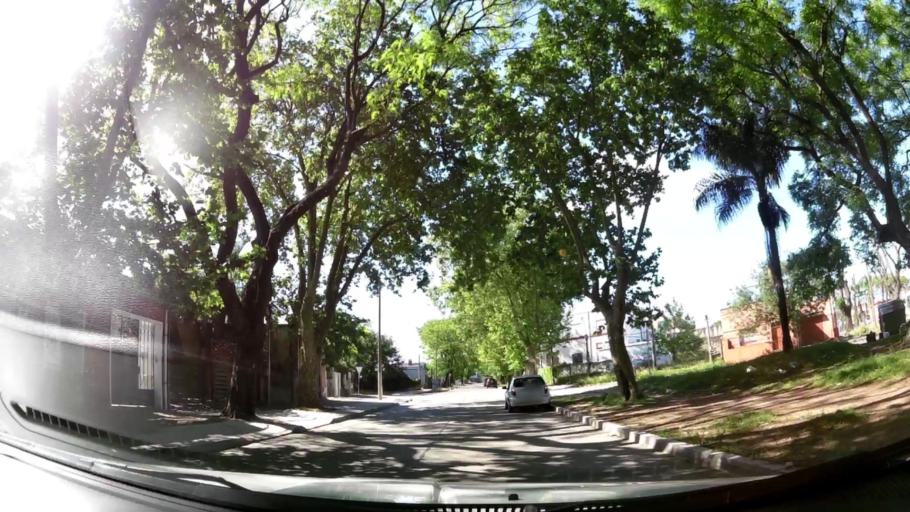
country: UY
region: Montevideo
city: Montevideo
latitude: -34.8496
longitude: -56.2129
